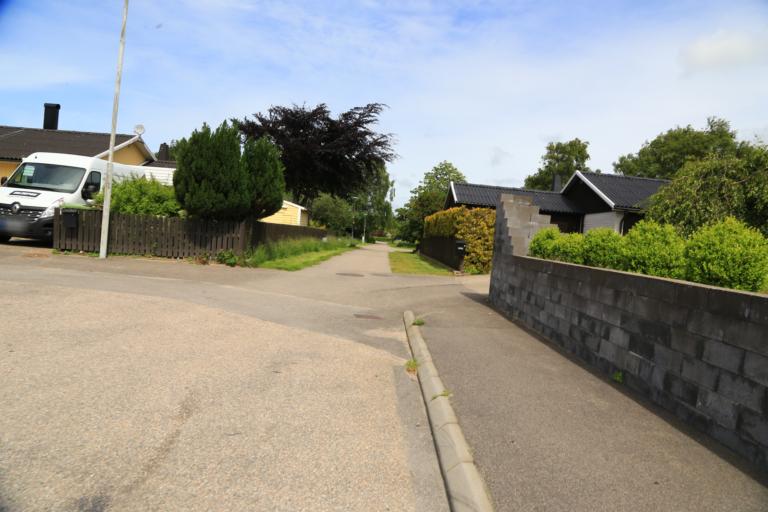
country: SE
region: Halland
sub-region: Varbergs Kommun
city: Varberg
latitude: 57.1077
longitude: 12.2803
